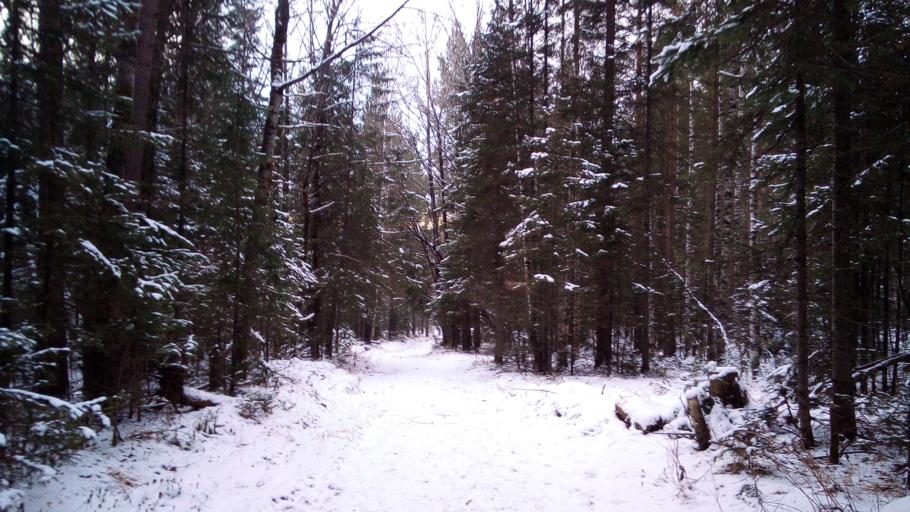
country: RU
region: Chelyabinsk
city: Satka
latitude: 54.8173
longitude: 59.0050
